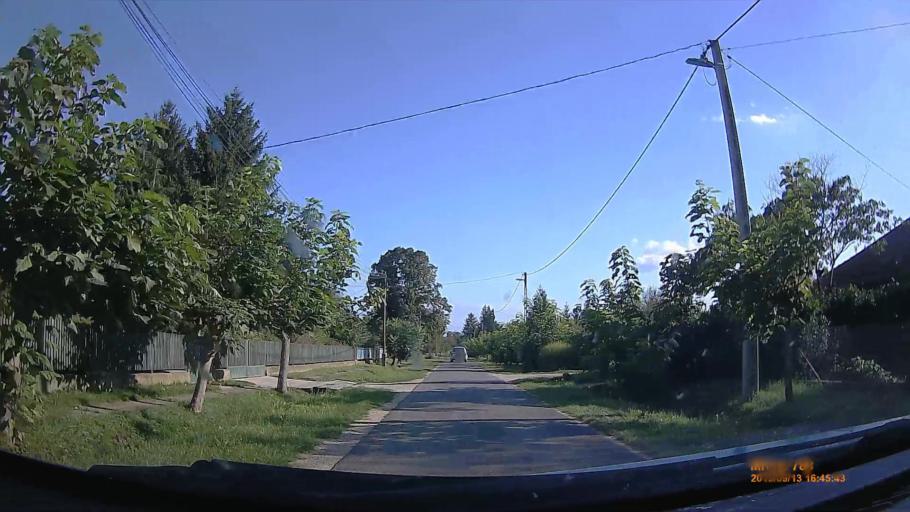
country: HU
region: Zala
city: Pacsa
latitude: 46.6232
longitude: 17.0581
